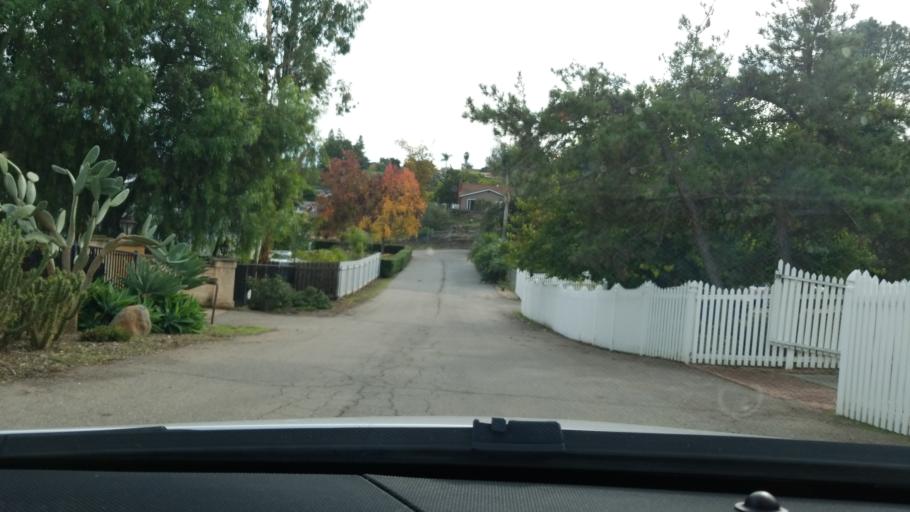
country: US
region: California
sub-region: San Diego County
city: Casa de Oro-Mount Helix
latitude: 32.7740
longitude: -116.9473
